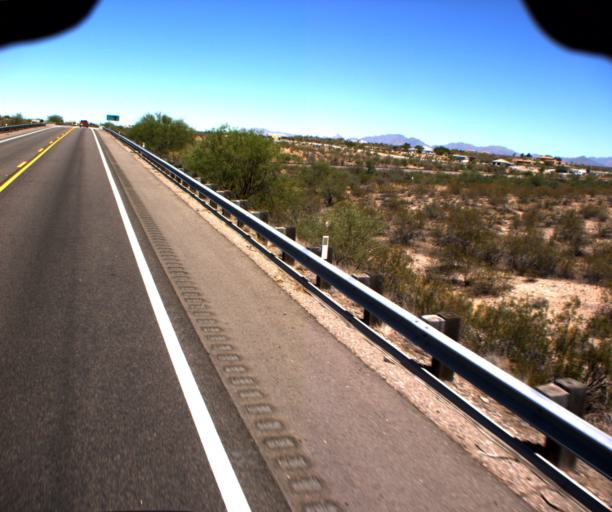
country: US
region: Arizona
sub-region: Maricopa County
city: Wickenburg
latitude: 34.0299
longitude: -112.8158
